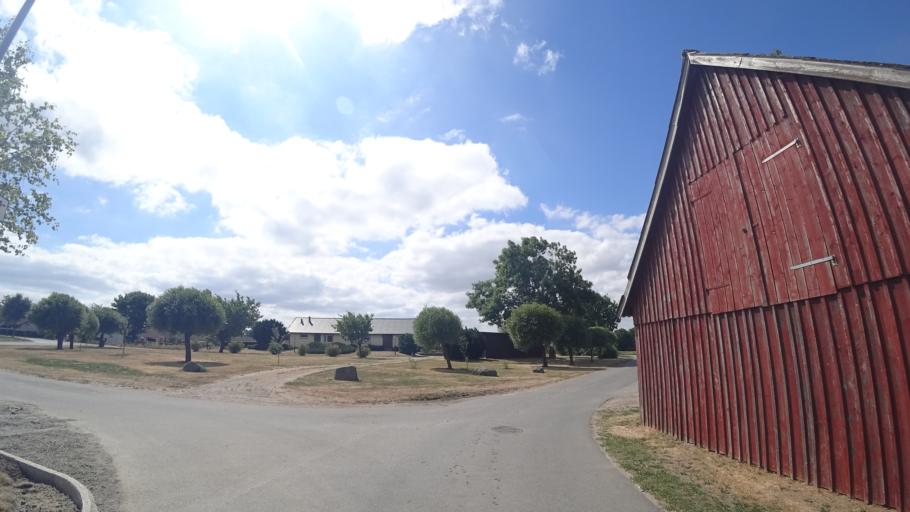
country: SE
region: Skane
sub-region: Kristianstads Kommun
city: Ahus
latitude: 55.9824
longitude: 14.2665
